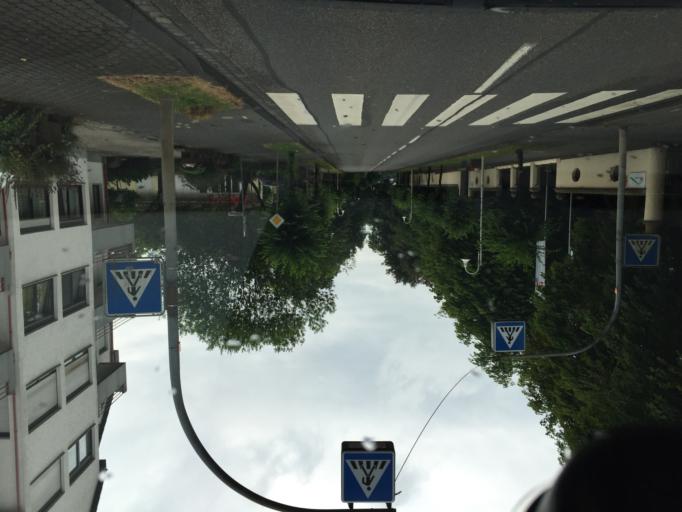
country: DE
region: Rheinland-Pfalz
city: Rengsdorf
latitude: 50.5004
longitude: 7.4976
